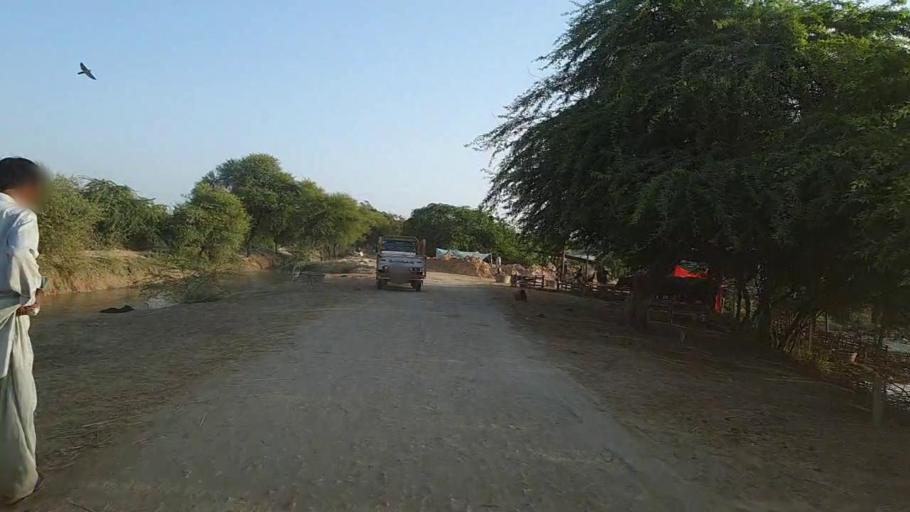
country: PK
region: Sindh
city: Kario
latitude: 24.6918
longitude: 68.6726
